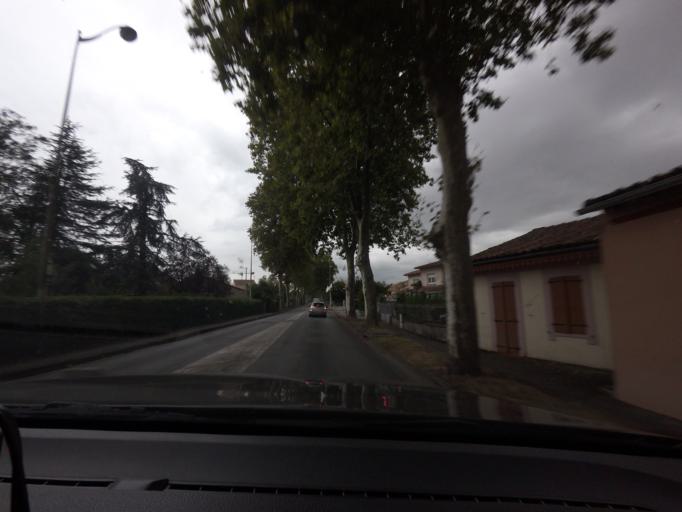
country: FR
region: Midi-Pyrenees
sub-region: Departement de la Haute-Garonne
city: Tournefeuille
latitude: 43.5843
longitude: 1.3433
